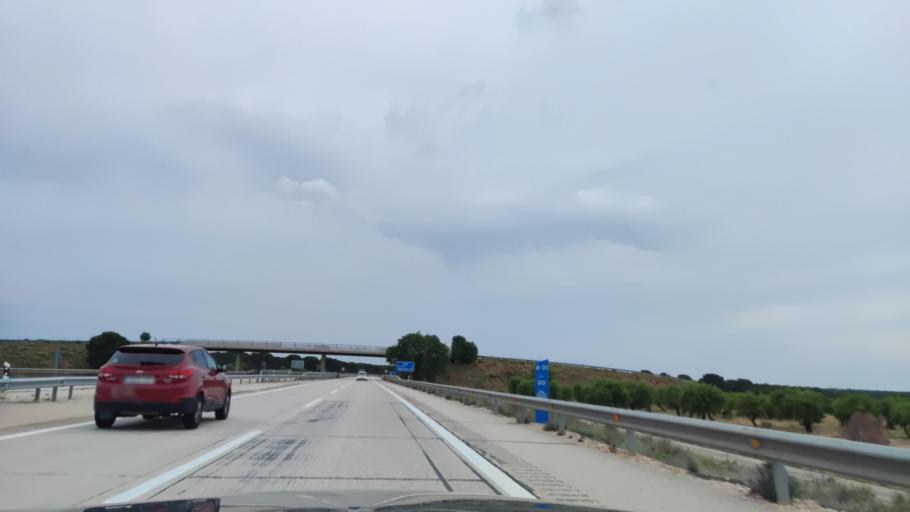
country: ES
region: Castille-La Mancha
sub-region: Provincia de Cuenca
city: Pozoamargo
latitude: 39.3523
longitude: -2.2027
